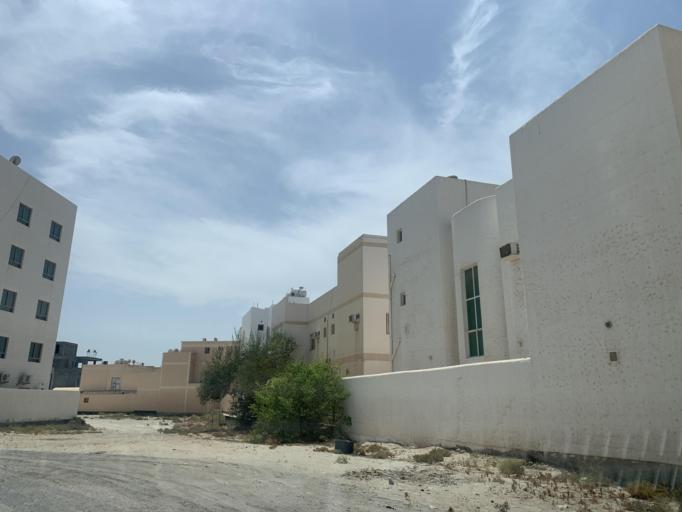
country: BH
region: Northern
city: Madinat `Isa
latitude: 26.1888
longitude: 50.4797
